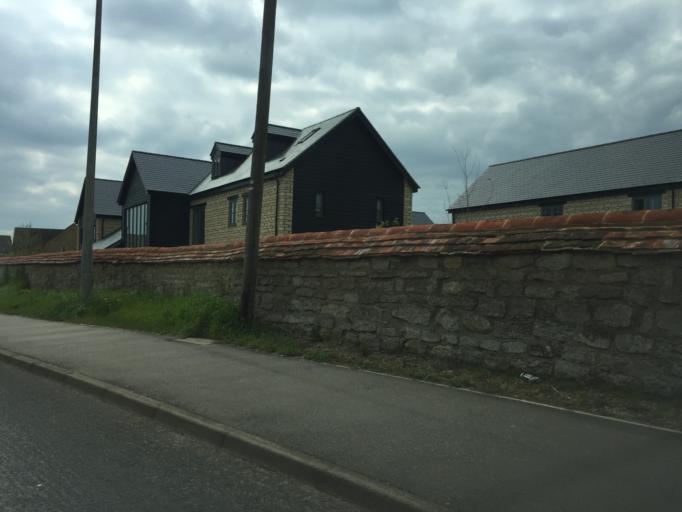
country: GB
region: England
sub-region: Milton Keynes
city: Bradwell
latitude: 52.0708
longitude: -0.7716
